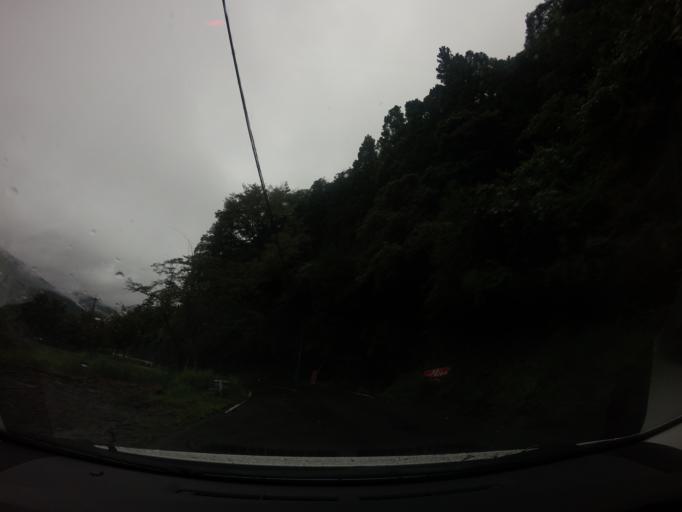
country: JP
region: Wakayama
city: Koya
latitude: 34.0632
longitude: 135.7523
